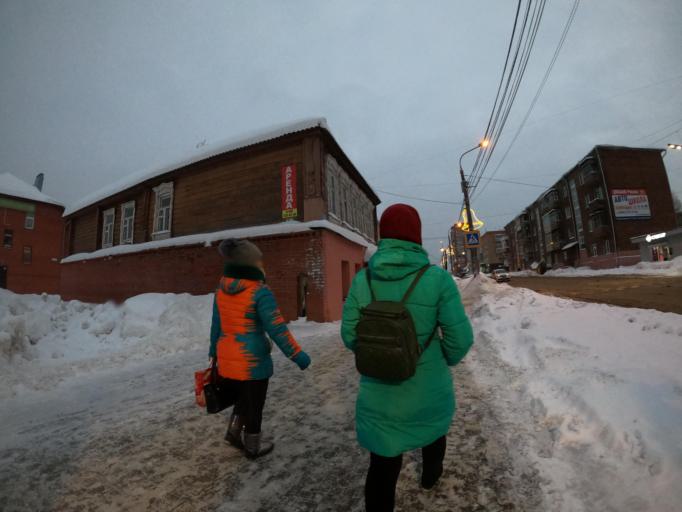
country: RU
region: Moskovskaya
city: Pavlovskiy Posad
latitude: 55.7797
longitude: 38.6712
